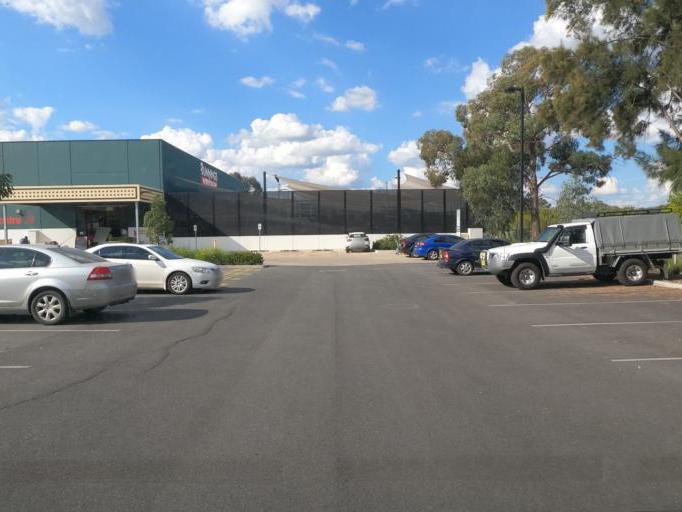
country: AU
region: New South Wales
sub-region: Albury Municipality
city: East Albury
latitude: -36.0748
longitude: 146.9490
